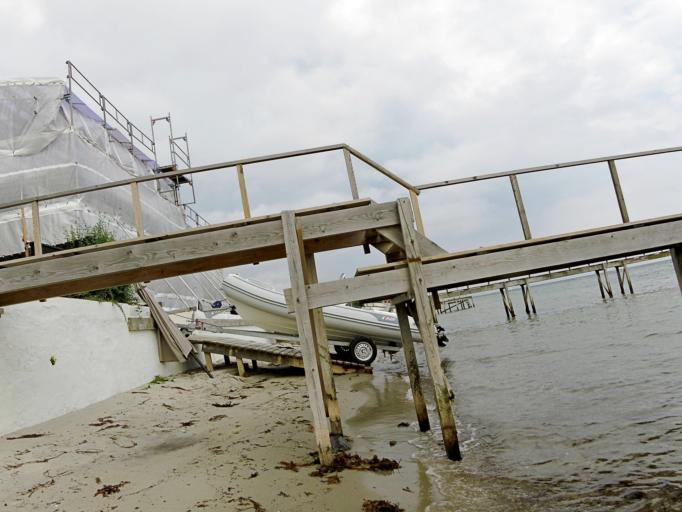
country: DK
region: Capital Region
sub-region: Gentofte Kommune
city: Charlottenlund
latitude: 55.7836
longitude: 12.5939
